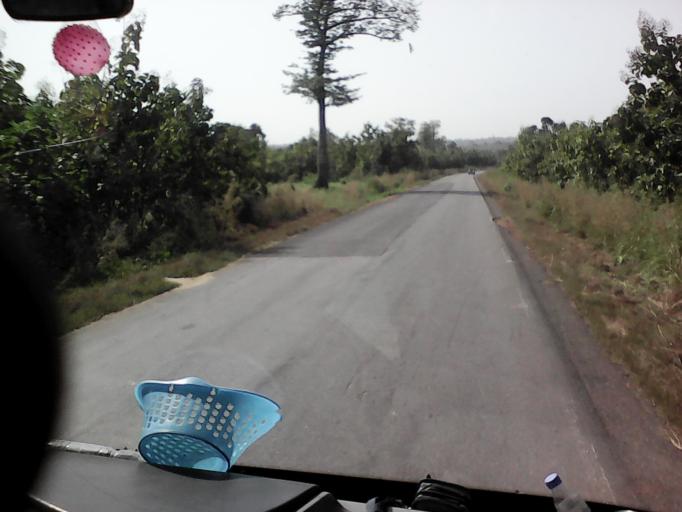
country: TG
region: Centrale
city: Sotouboua
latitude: 8.7538
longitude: 1.0570
